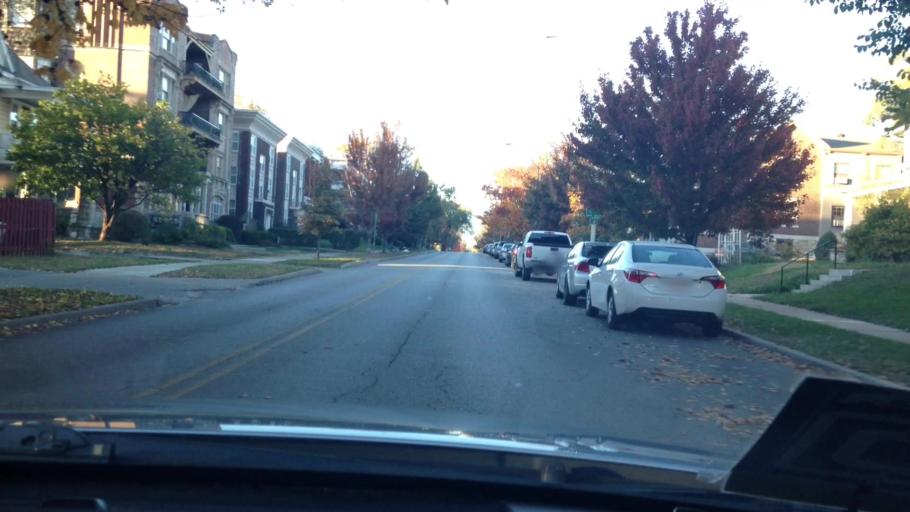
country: US
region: Kansas
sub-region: Johnson County
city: Westwood
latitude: 39.0495
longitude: -94.5842
